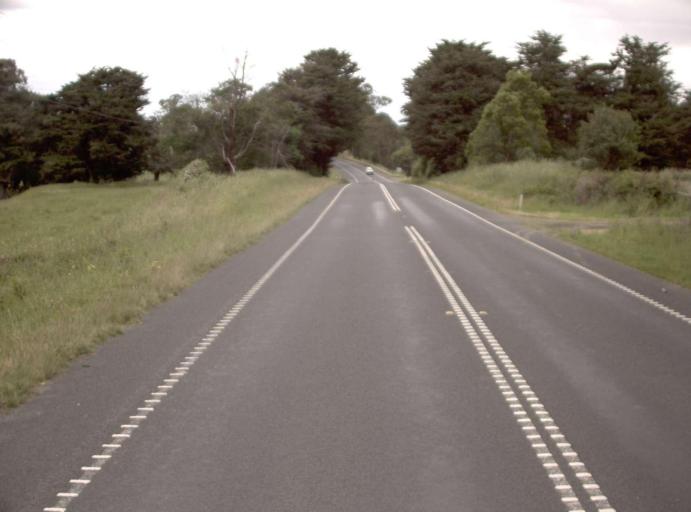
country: AU
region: Victoria
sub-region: Bass Coast
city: North Wonthaggi
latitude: -38.4461
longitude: 145.8535
